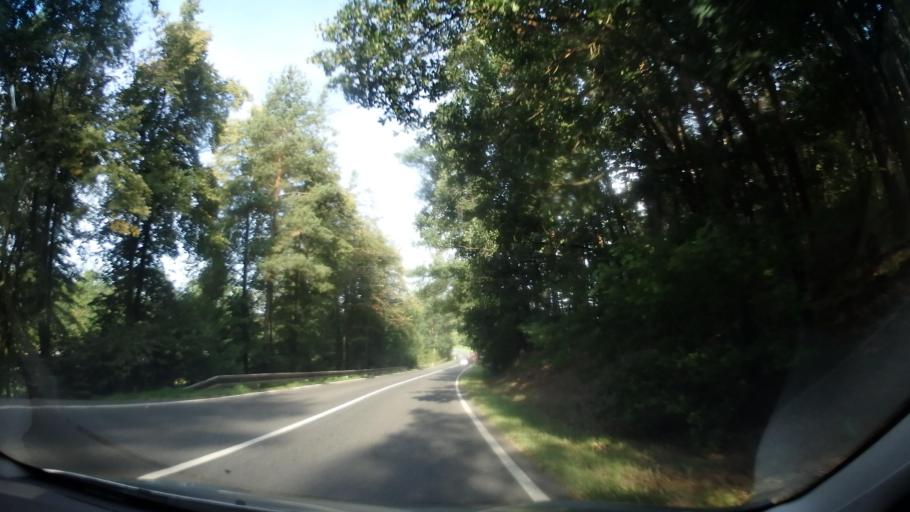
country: CZ
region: Jihocesky
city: Cimelice
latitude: 49.4378
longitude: 14.1298
